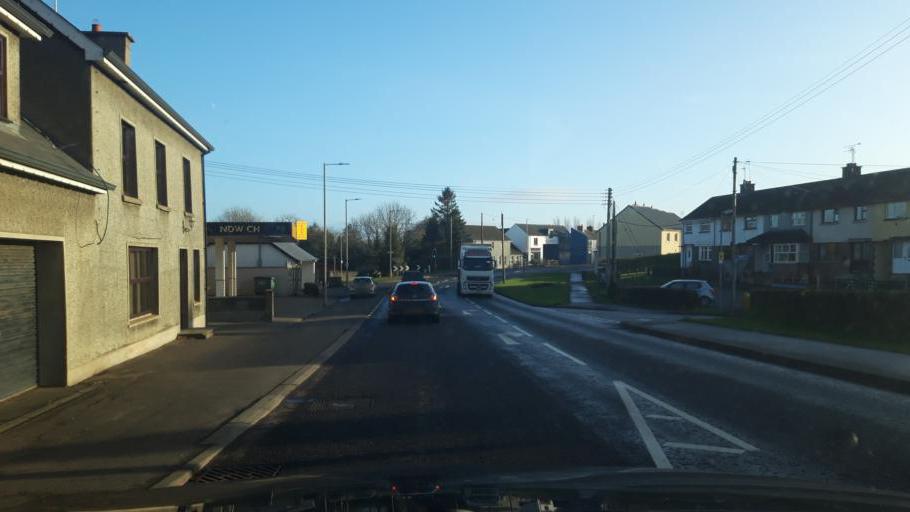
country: GB
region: Northern Ireland
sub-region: Magherafelt District
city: Magherafelt
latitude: 54.7709
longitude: -6.6744
